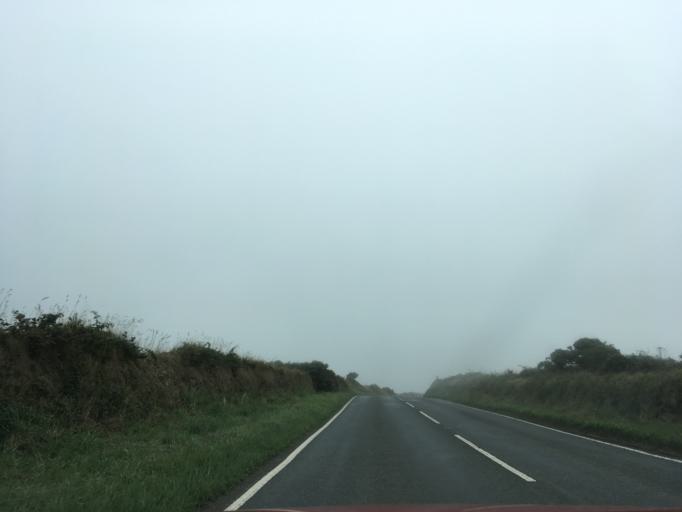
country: GB
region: Wales
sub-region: Pembrokeshire
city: Saint David's
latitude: 51.8804
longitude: -5.2235
